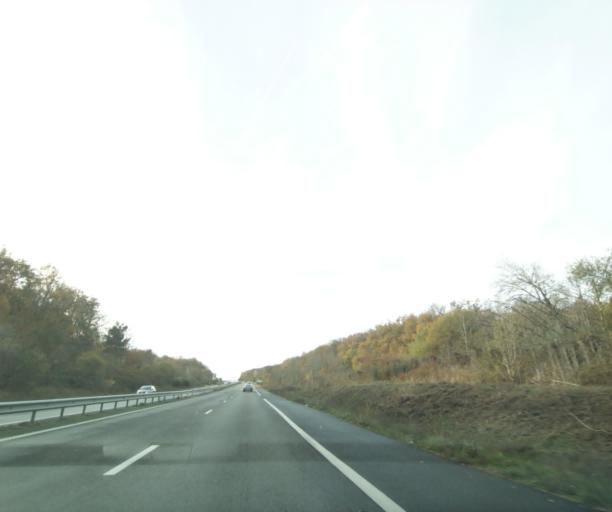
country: FR
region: Midi-Pyrenees
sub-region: Departement du Gers
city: Pujaudran
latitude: 43.5864
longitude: 1.1544
